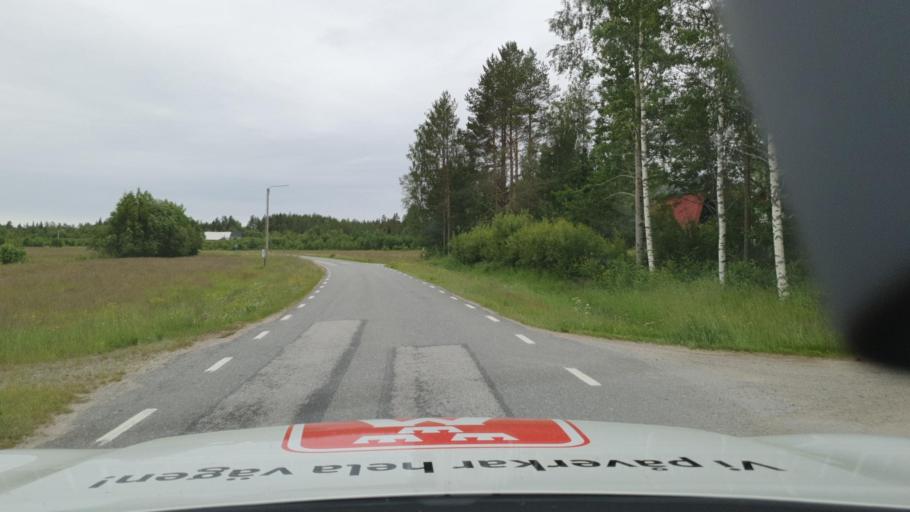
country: SE
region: Vaesterbotten
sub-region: Nordmalings Kommun
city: Nordmaling
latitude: 63.5025
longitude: 19.4171
